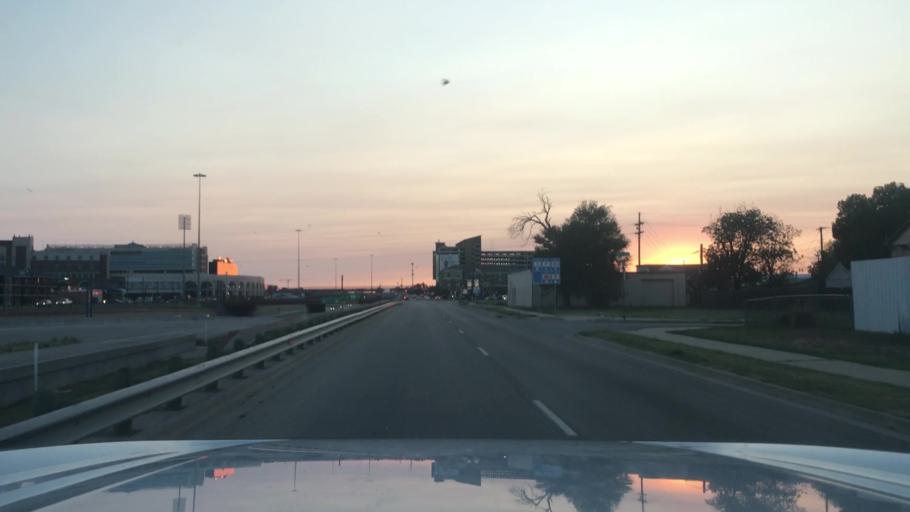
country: US
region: Texas
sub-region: Lubbock County
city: Lubbock
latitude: 33.5931
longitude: -101.8669
